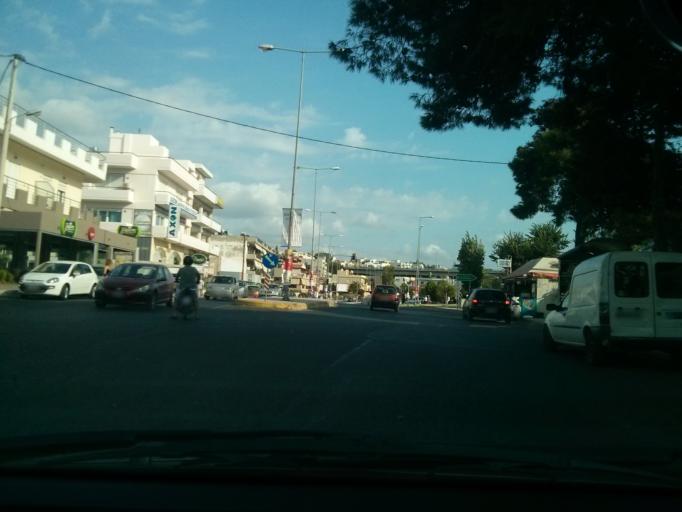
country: GR
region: Crete
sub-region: Nomos Irakleiou
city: Irakleion
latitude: 35.3231
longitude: 25.1412
